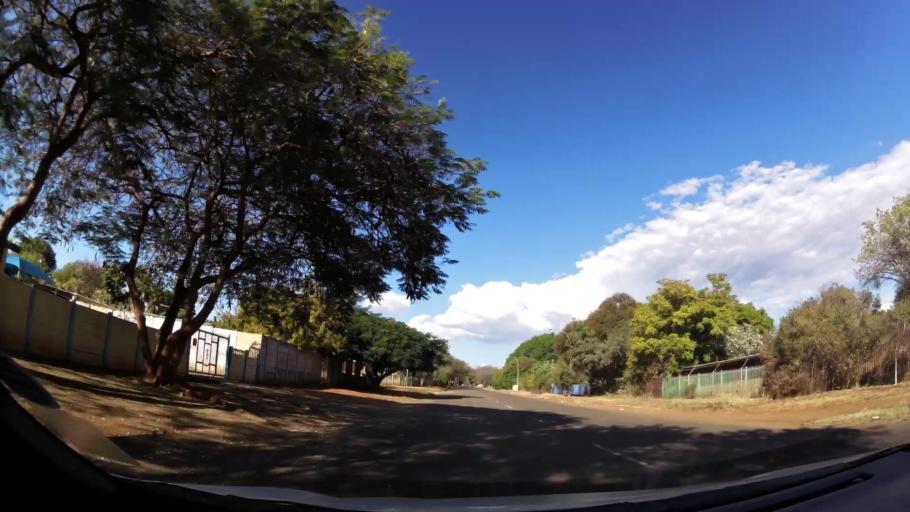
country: ZA
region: Limpopo
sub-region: Waterberg District Municipality
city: Mokopane
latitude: -24.1867
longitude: 28.9944
